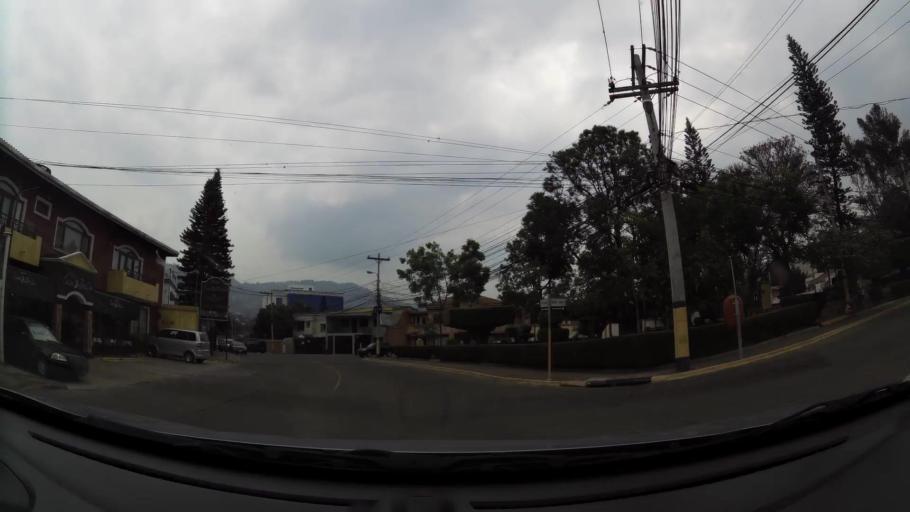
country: HN
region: Francisco Morazan
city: Tegucigalpa
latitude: 14.1020
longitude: -87.1937
